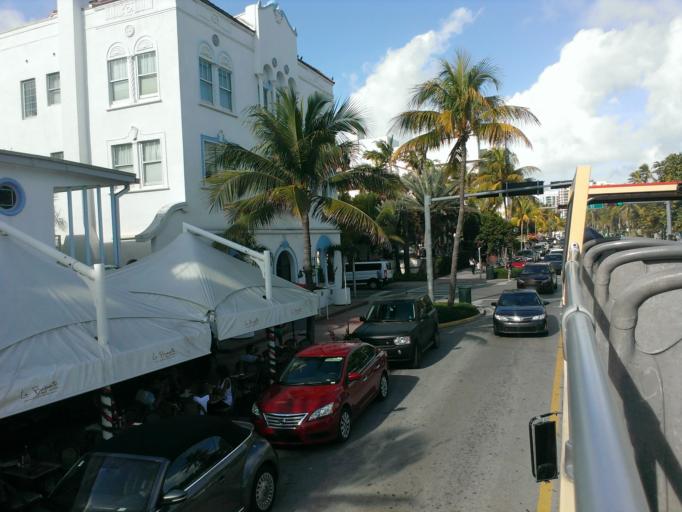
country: US
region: Florida
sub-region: Miami-Dade County
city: Miami Beach
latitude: 25.7812
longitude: -80.1305
